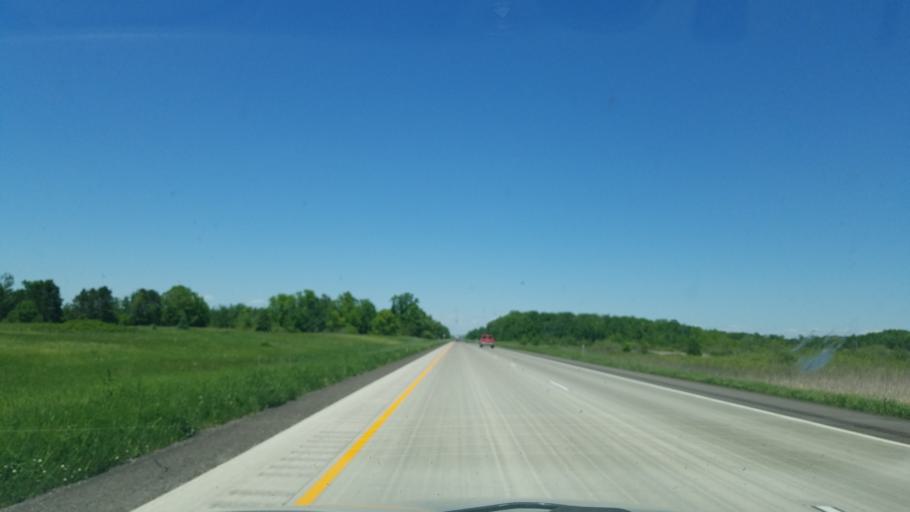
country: US
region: Minnesota
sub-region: Pine County
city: Pine City
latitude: 45.8716
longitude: -92.9697
